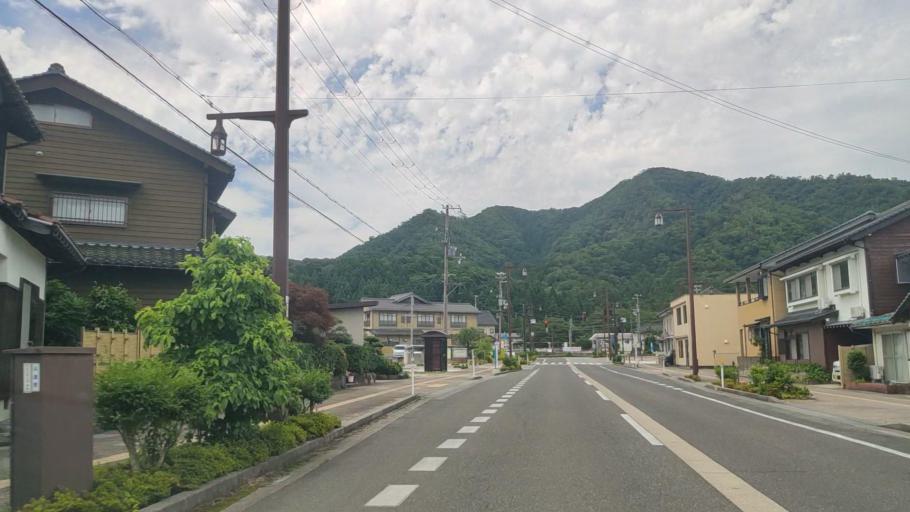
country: JP
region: Hyogo
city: Toyooka
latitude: 35.6510
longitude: 134.7578
